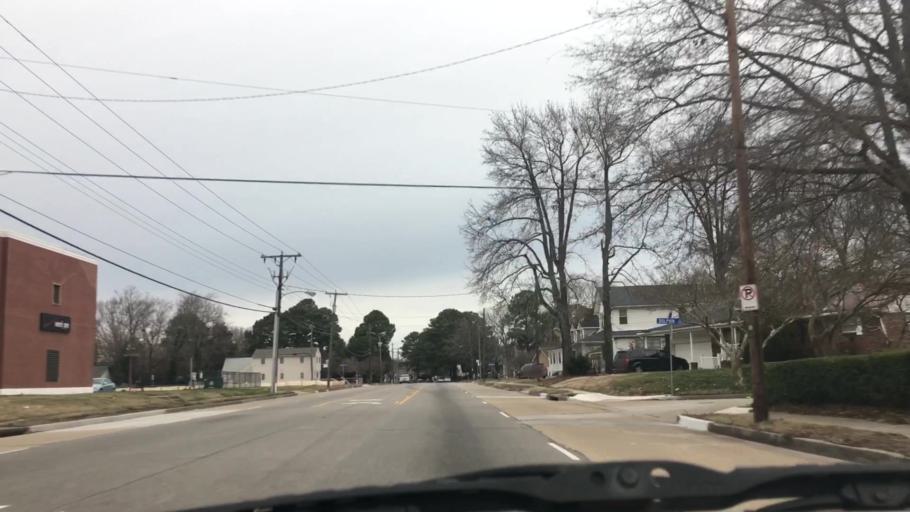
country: US
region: Virginia
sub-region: City of Norfolk
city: Norfolk
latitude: 36.8803
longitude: -76.2336
